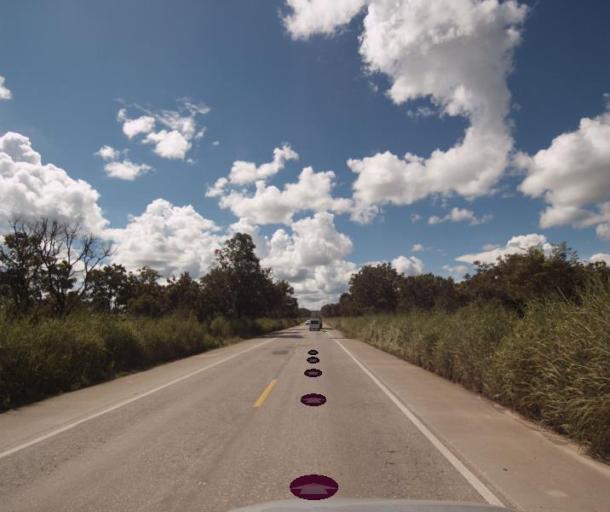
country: BR
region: Goias
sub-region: Porangatu
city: Porangatu
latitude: -13.5870
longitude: -49.0416
